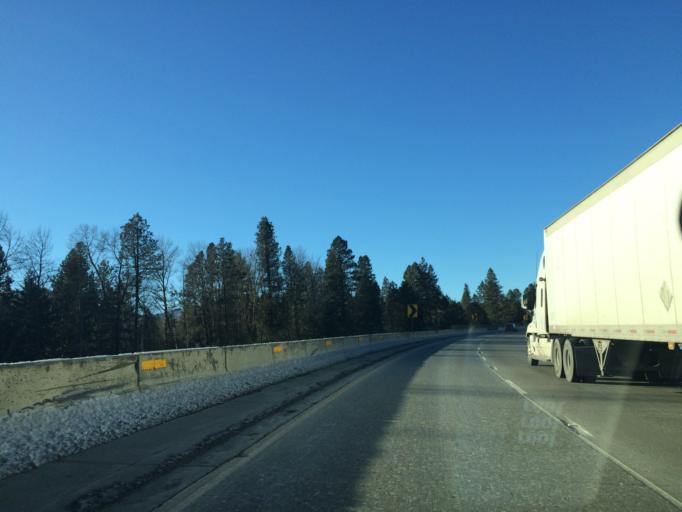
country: US
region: Washington
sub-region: Kittitas County
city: Cle Elum
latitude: 47.1824
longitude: -121.0382
